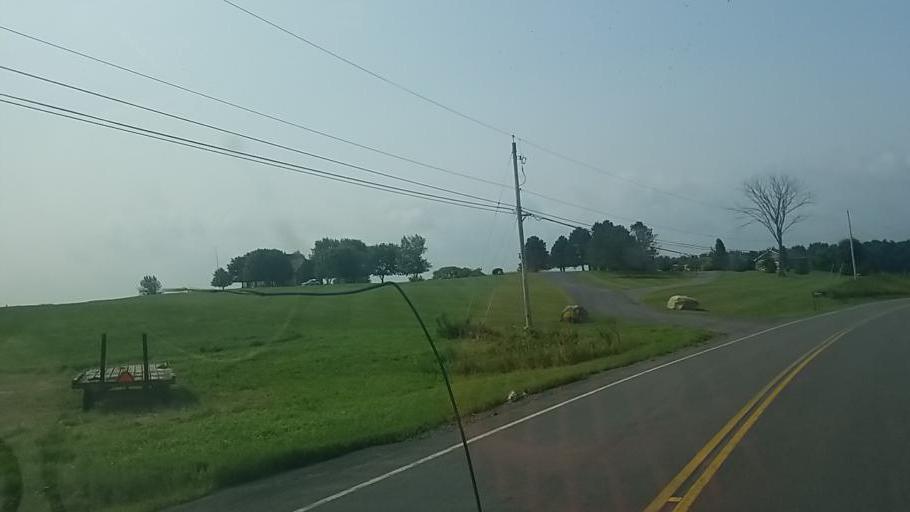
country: US
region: New York
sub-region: Fulton County
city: Johnstown
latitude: 42.9996
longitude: -74.4070
